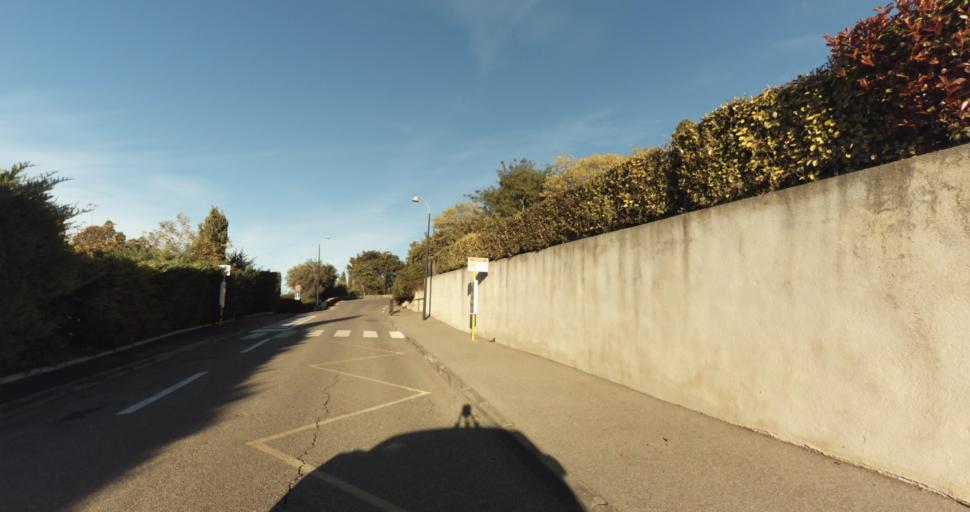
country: FR
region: Provence-Alpes-Cote d'Azur
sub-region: Departement des Bouches-du-Rhone
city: Venelles
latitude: 43.5986
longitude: 5.4785
